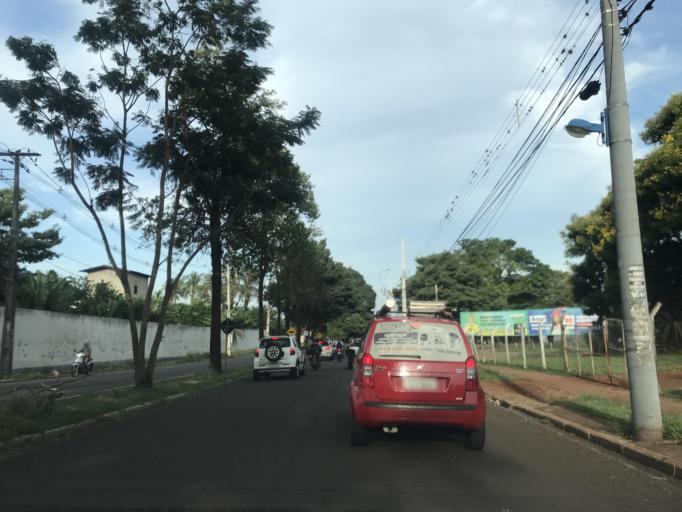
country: BR
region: Parana
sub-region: Maringa
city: Maringa
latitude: -23.4248
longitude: -51.9690
